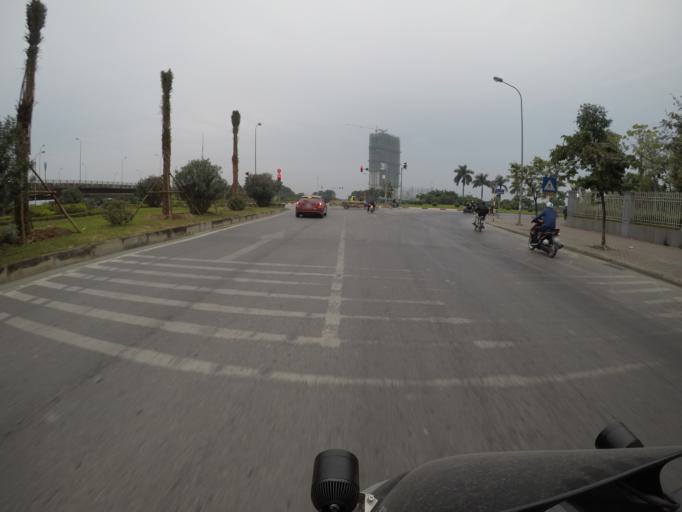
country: VN
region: Ha Noi
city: Thanh Xuan
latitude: 21.0048
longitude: 105.7741
